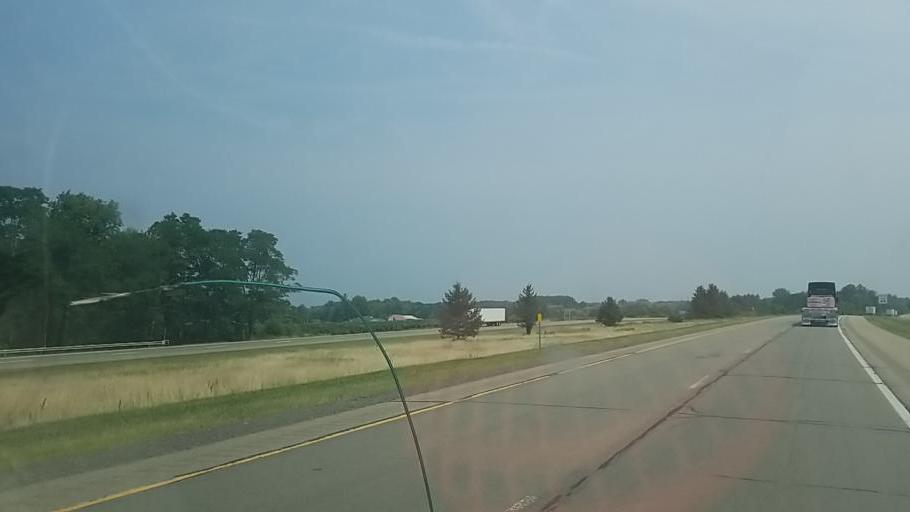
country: US
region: New York
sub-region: Chautauqua County
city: Westfield
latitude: 42.3408
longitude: -79.5777
